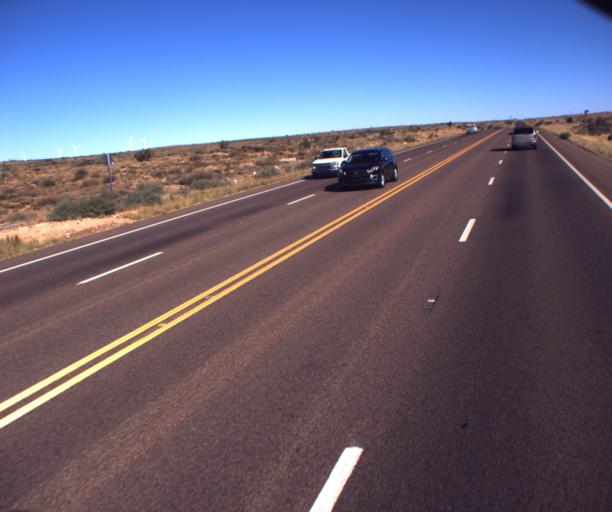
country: US
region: Arizona
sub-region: Navajo County
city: Snowflake
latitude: 34.5830
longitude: -110.0848
